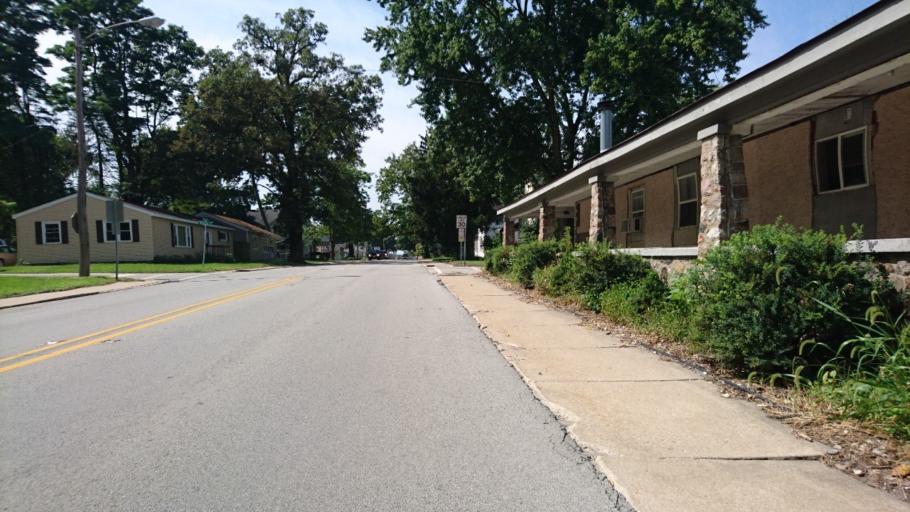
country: US
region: Illinois
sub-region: Will County
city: Wilmington
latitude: 41.3100
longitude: -88.1400
